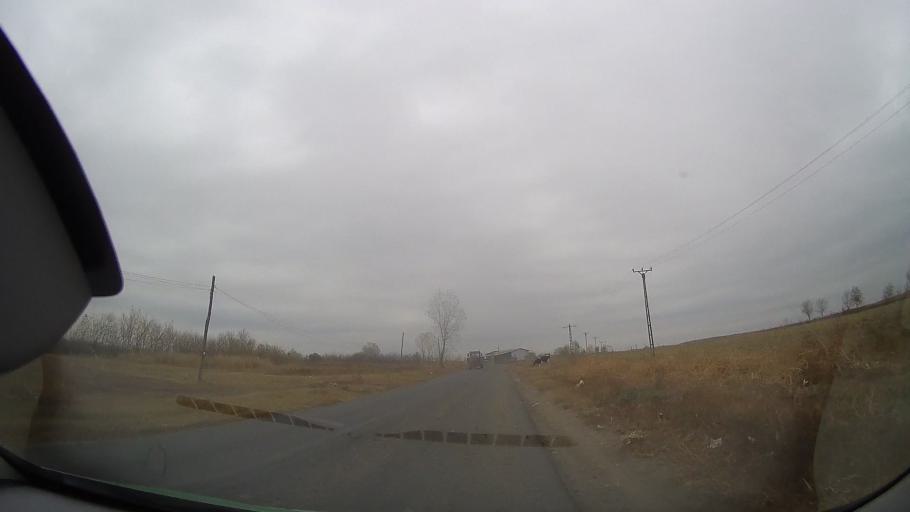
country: RO
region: Braila
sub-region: Comuna Ciocile
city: Ciocile
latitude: 44.8194
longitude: 27.2539
